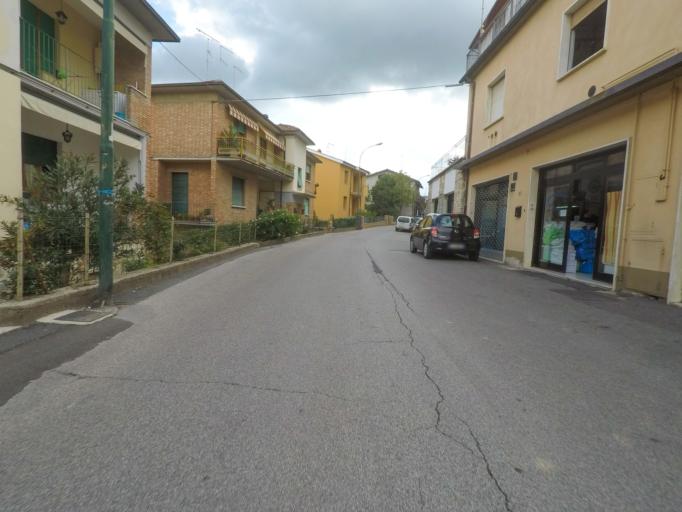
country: IT
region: Tuscany
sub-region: Provincia di Siena
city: Montepulciano
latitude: 43.0998
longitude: 11.7869
